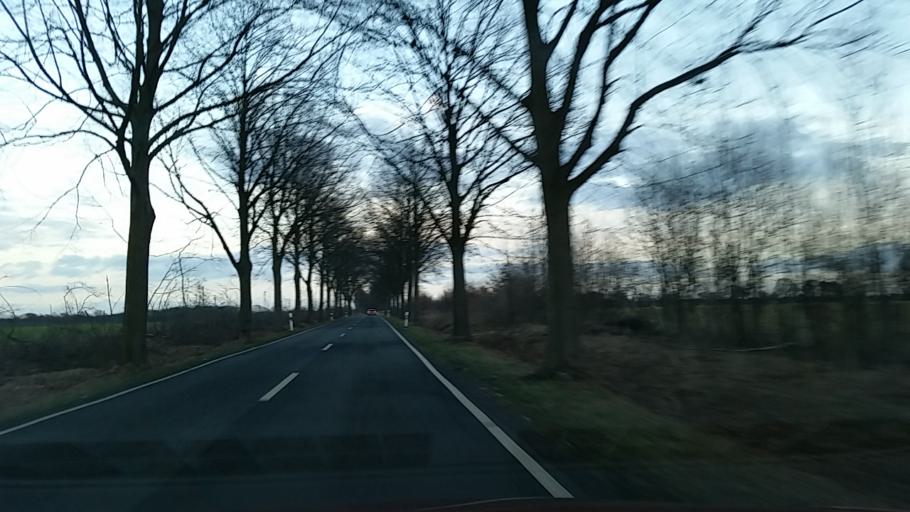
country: DE
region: Lower Saxony
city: Tiddische
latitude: 52.4807
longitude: 10.8062
